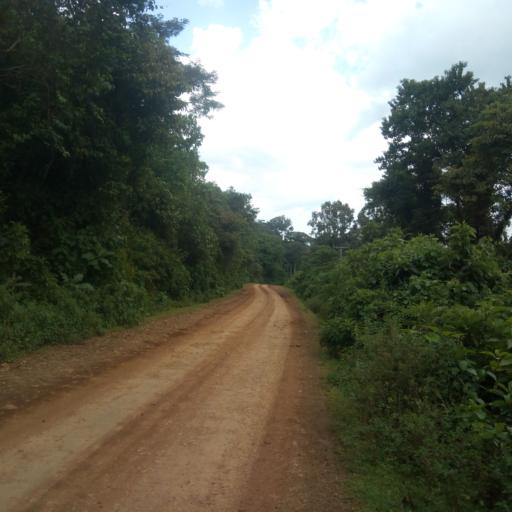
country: ET
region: Oromiya
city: Gore
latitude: 7.7895
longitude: 35.4562
